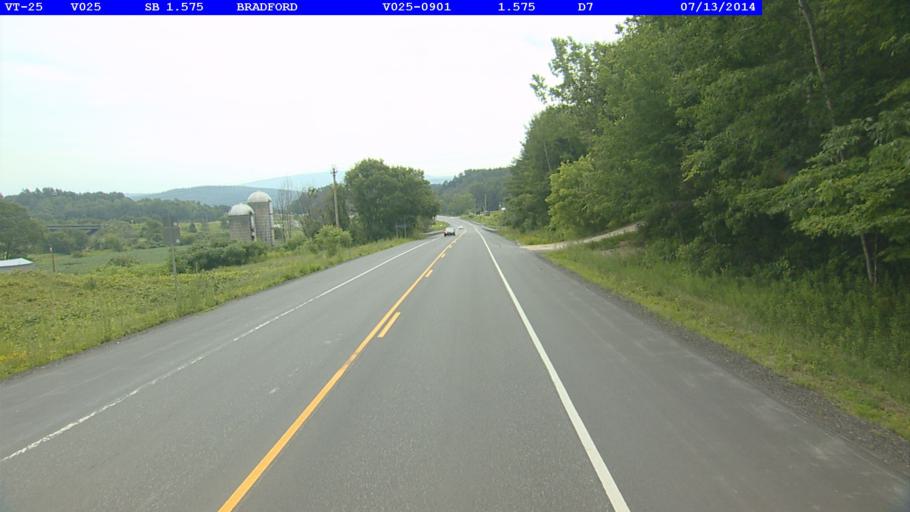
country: US
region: New Hampshire
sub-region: Grafton County
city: Orford
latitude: 43.9855
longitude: -72.1404
